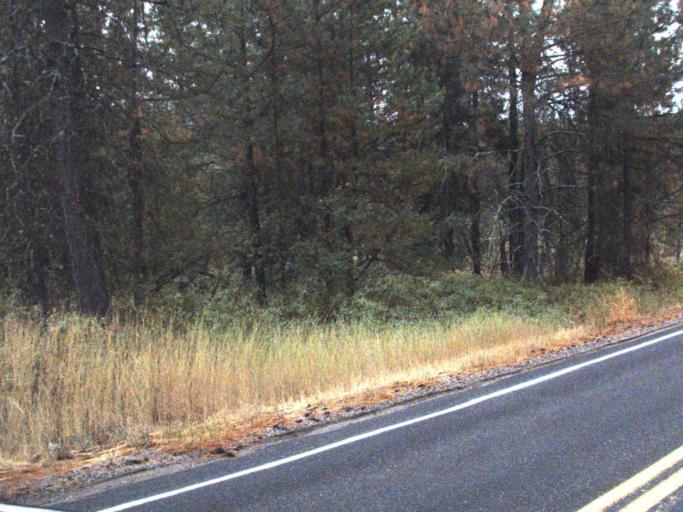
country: US
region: Washington
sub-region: Stevens County
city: Chewelah
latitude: 48.0457
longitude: -117.7415
